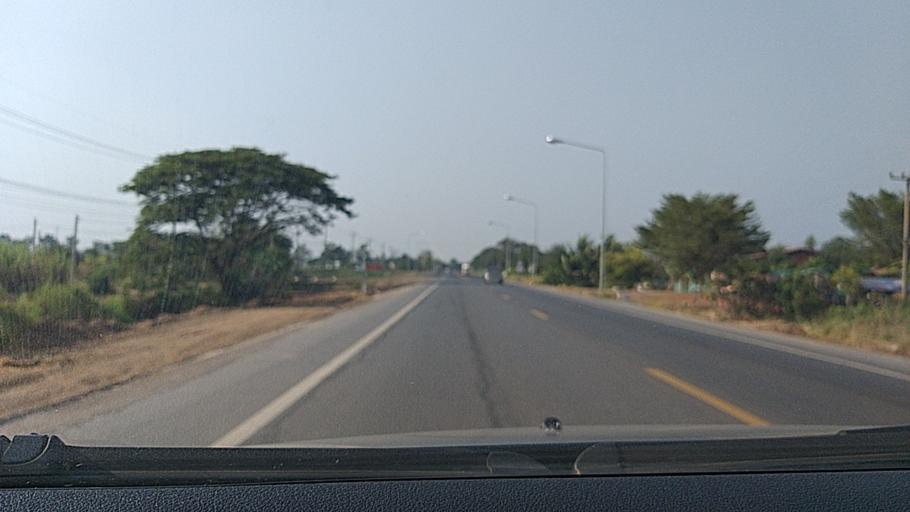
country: TH
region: Sing Buri
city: Phrom Buri
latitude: 14.7739
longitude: 100.4368
